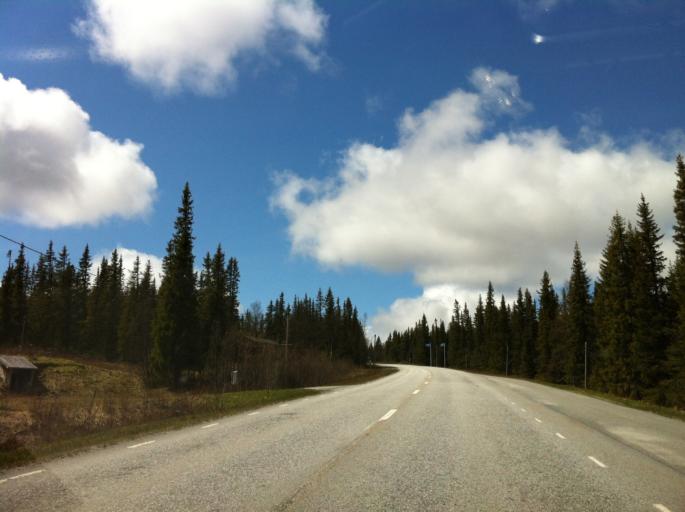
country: NO
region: Hedmark
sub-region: Engerdal
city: Engerdal
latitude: 62.5400
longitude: 12.4546
